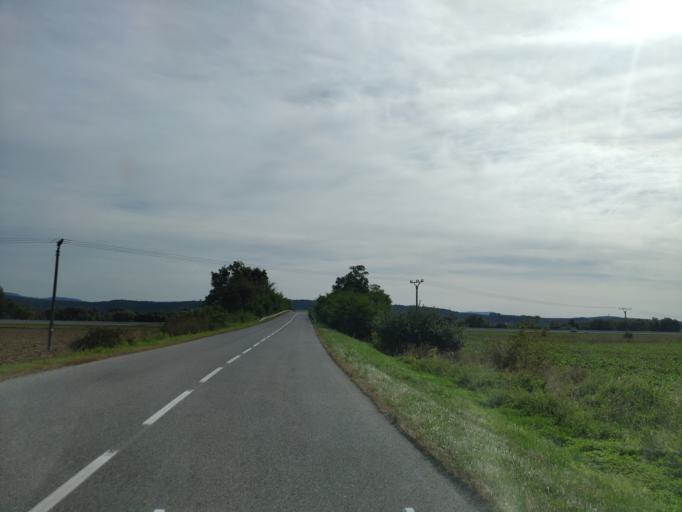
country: SK
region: Kosicky
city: Kosice
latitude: 48.8165
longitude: 21.3073
